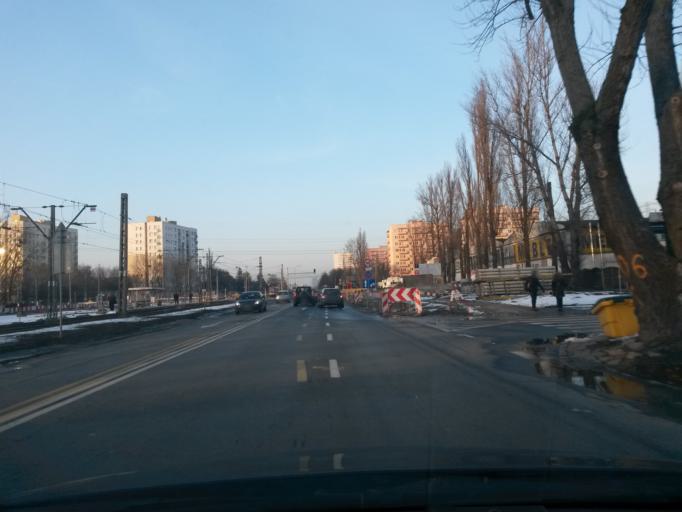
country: PL
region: Masovian Voivodeship
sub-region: Warszawa
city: Mokotow
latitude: 52.1875
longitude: 21.0023
